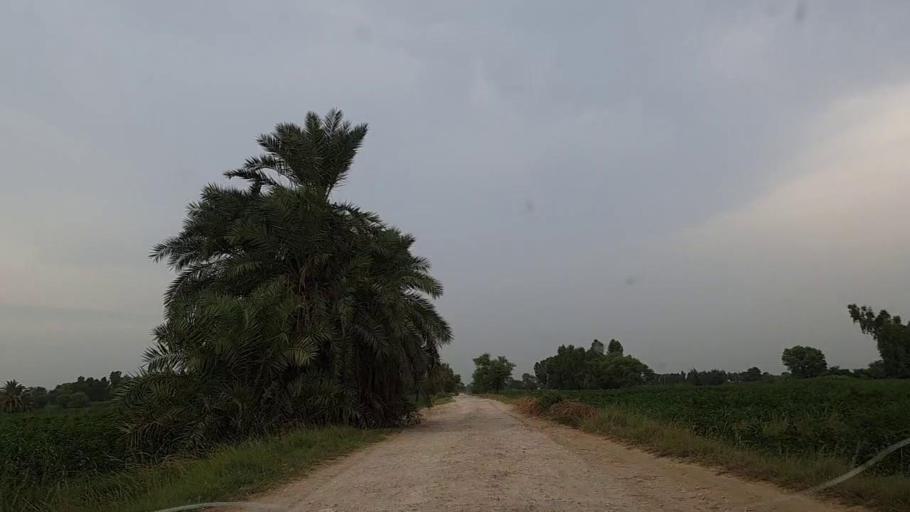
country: PK
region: Sindh
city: Khanpur
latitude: 27.8334
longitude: 69.6132
